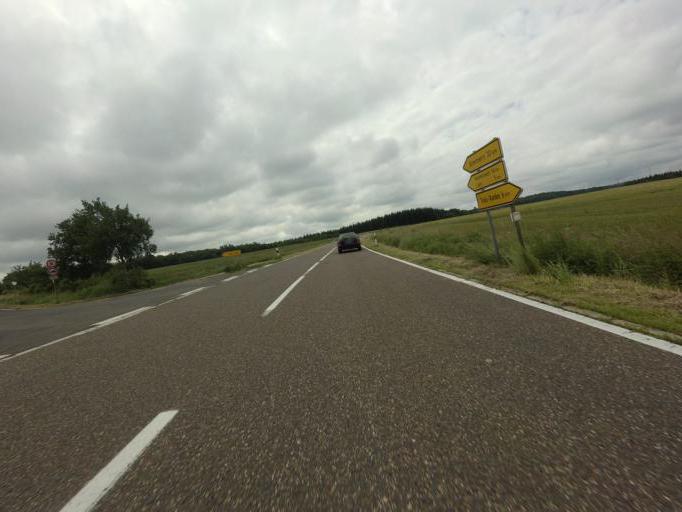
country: DE
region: Rheinland-Pfalz
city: Lutz
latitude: 50.1546
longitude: 7.3379
